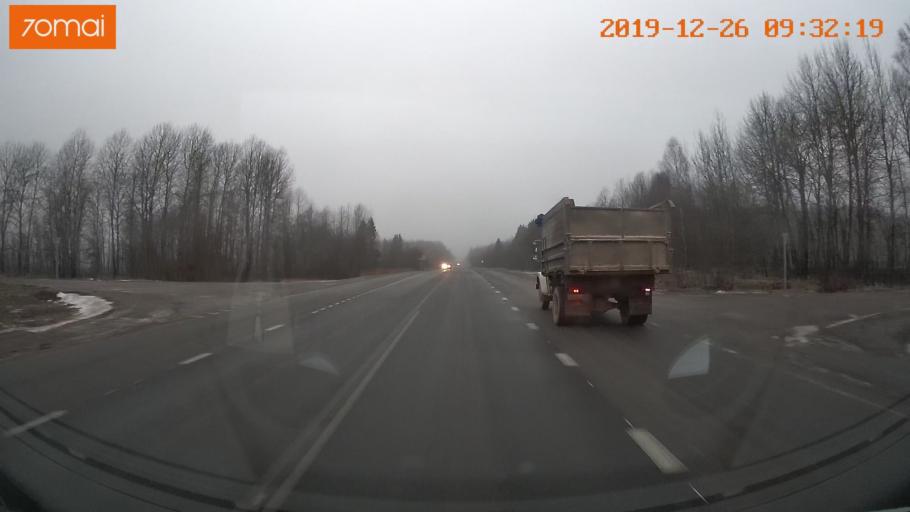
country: RU
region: Vologda
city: Gryazovets
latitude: 59.0765
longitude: 40.1183
